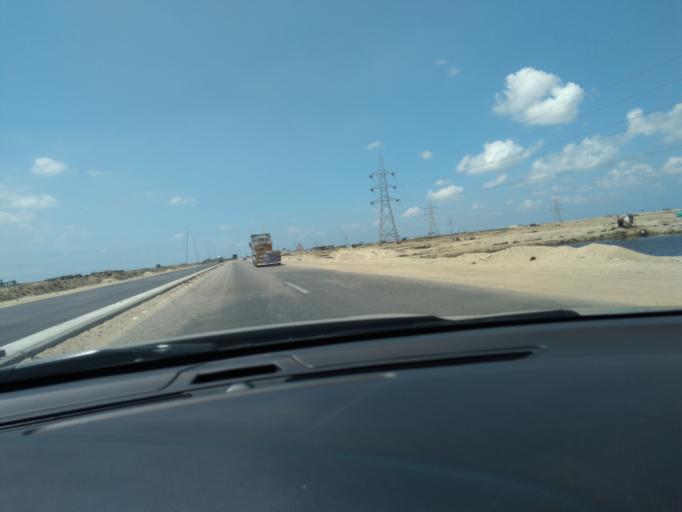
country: EG
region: Muhafazat ad Daqahliyah
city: Al Matariyah
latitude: 31.3455
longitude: 32.0597
